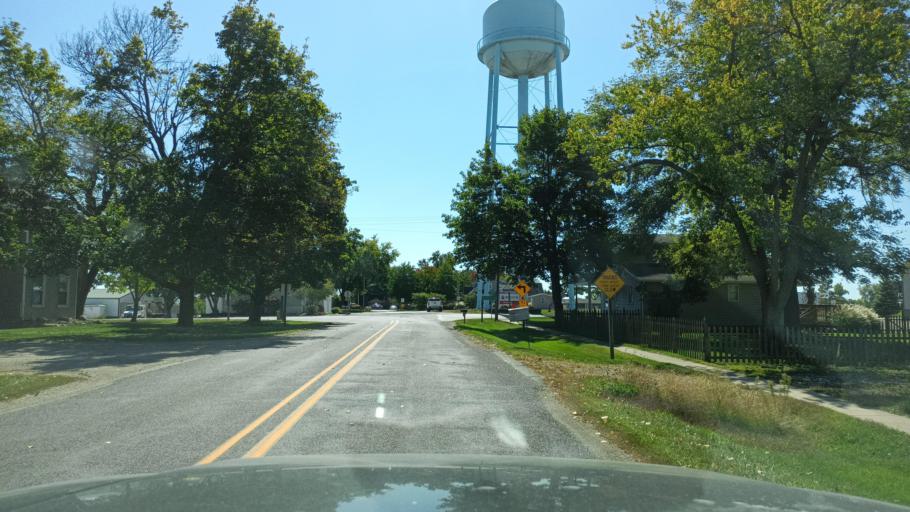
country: US
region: Illinois
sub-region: McLean County
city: Danvers
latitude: 40.6142
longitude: -89.2045
